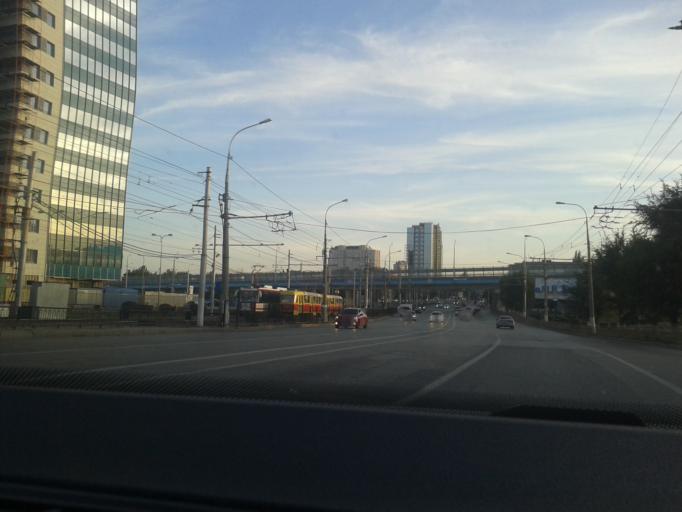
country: RU
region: Volgograd
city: Volgograd
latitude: 48.7281
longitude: 44.5383
